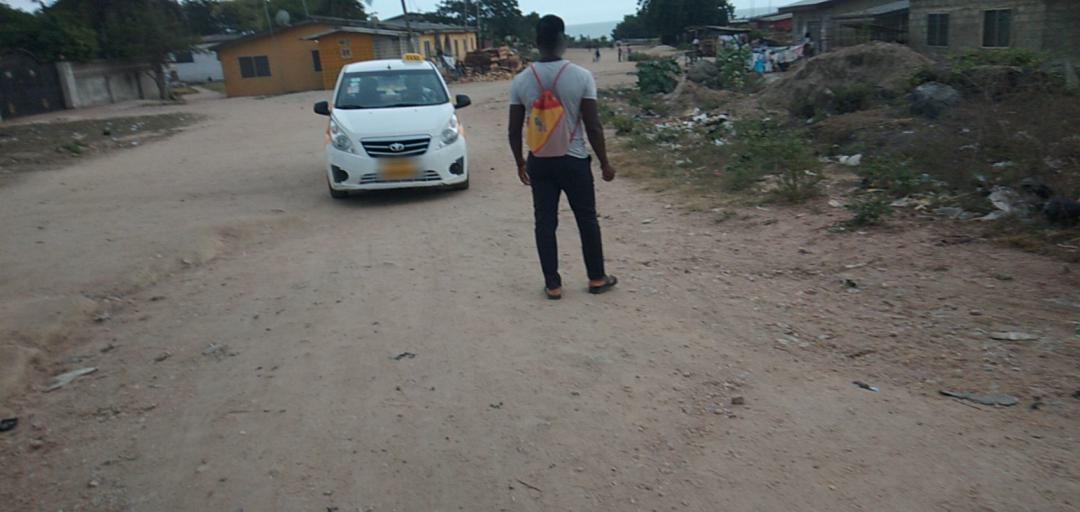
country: GH
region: Central
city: Winneba
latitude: 5.3534
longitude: -0.6152
